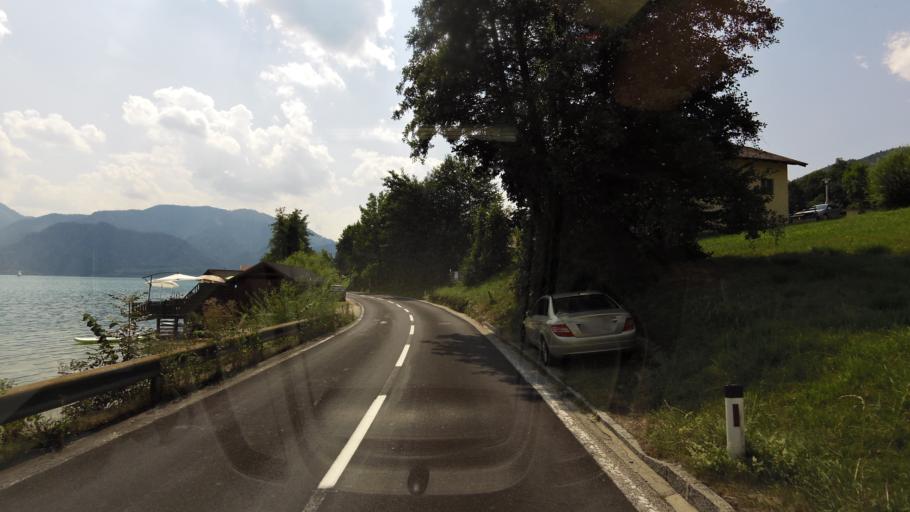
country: AT
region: Upper Austria
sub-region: Politischer Bezirk Vocklabruck
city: Steinbach am Attersee
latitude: 47.8319
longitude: 13.5197
